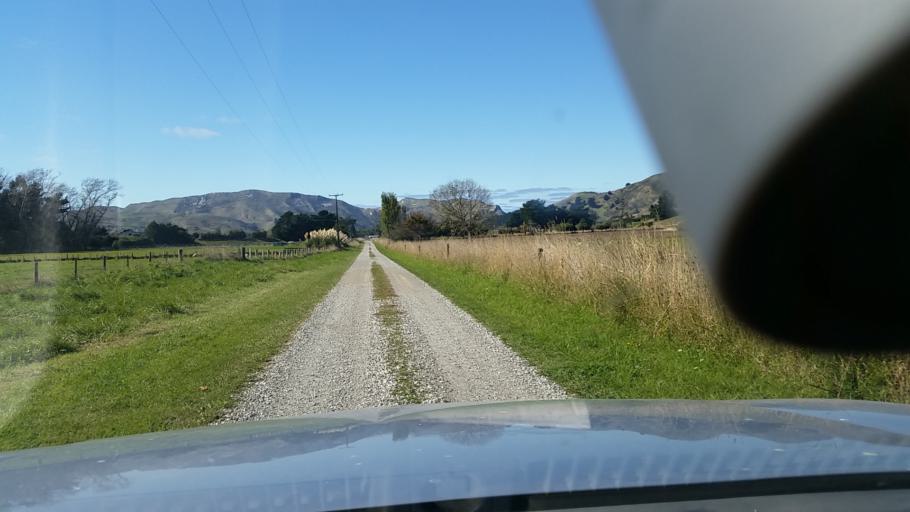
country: NZ
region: Marlborough
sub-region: Marlborough District
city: Blenheim
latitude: -41.8245
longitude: 174.1208
